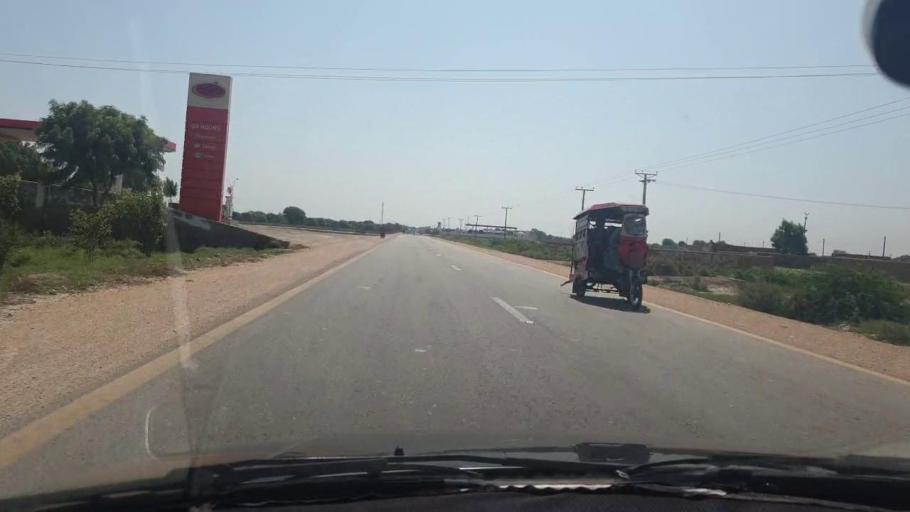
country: PK
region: Sindh
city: Chambar
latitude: 25.3126
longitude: 68.8057
